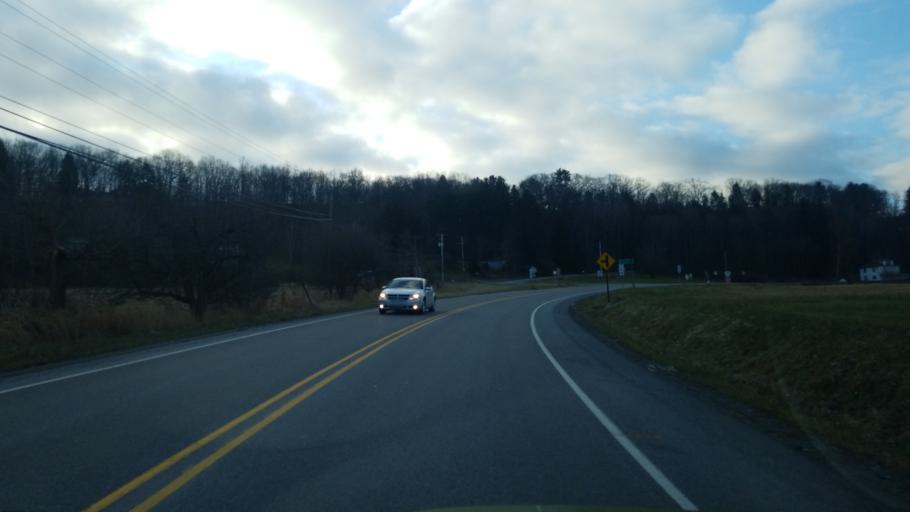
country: US
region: Pennsylvania
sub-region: Clearfield County
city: Clearfield
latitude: 41.0045
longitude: -78.4268
